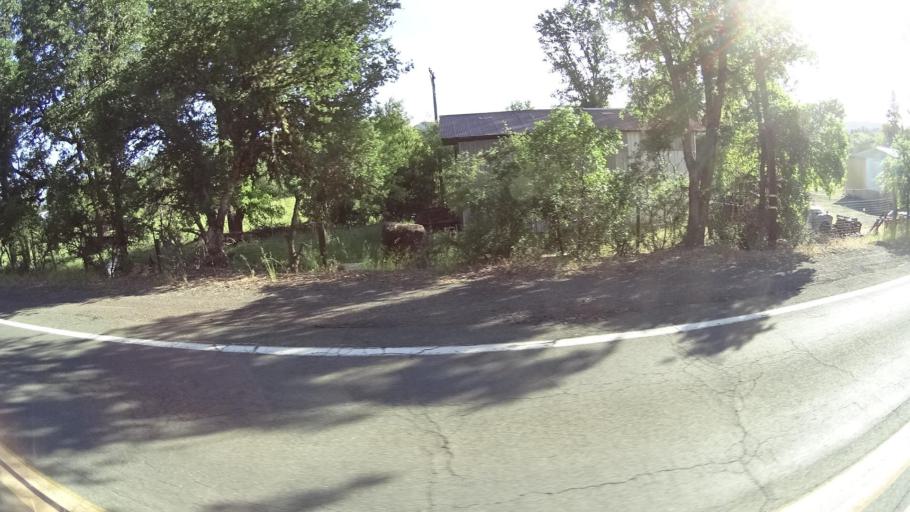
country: US
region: California
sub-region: Lake County
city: North Lakeport
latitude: 39.0947
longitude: -122.9660
